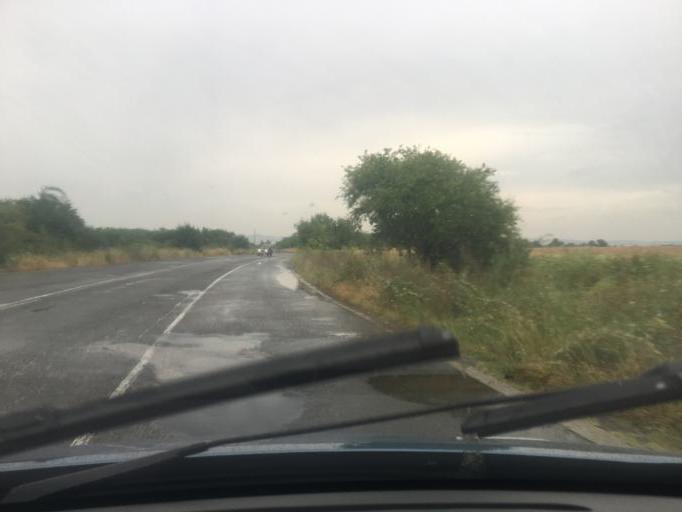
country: BG
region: Burgas
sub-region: Obshtina Burgas
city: Burgas
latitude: 42.5550
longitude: 27.4908
